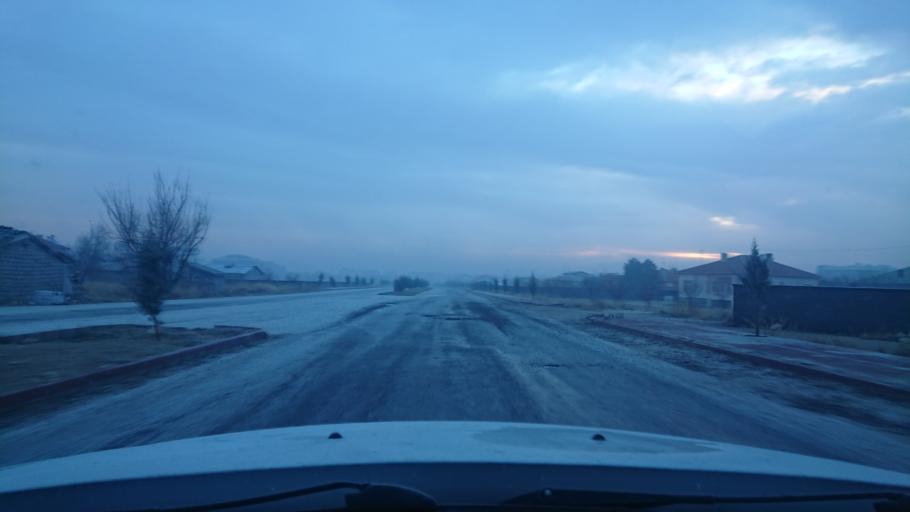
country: TR
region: Aksaray
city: Sultanhani
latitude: 38.2482
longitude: 33.5391
